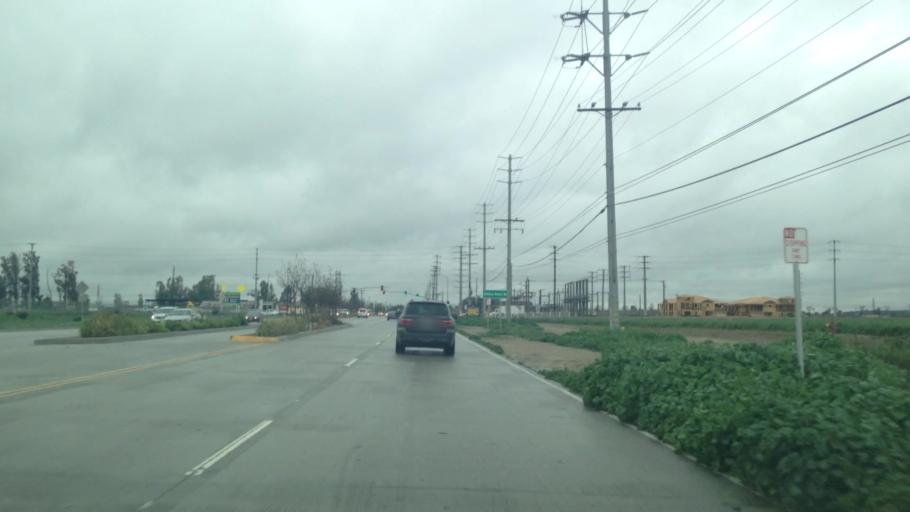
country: US
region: California
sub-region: Riverside County
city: Mira Loma
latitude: 33.9946
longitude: -117.5932
